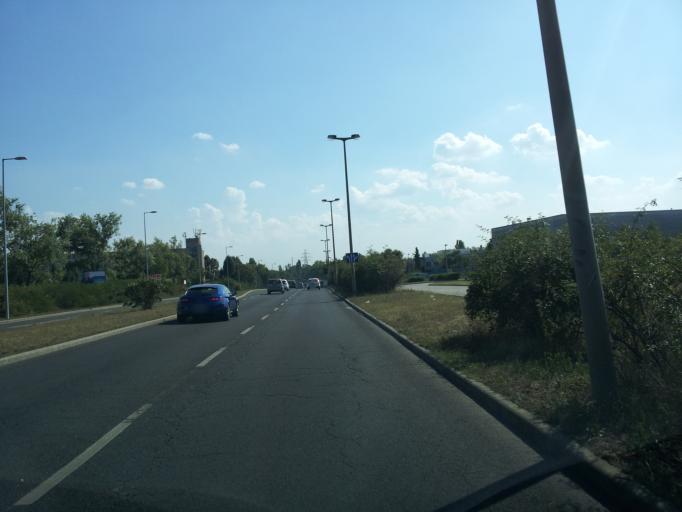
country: HU
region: Budapest
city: Budapest XXII. keruelet
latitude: 47.4495
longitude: 19.0444
